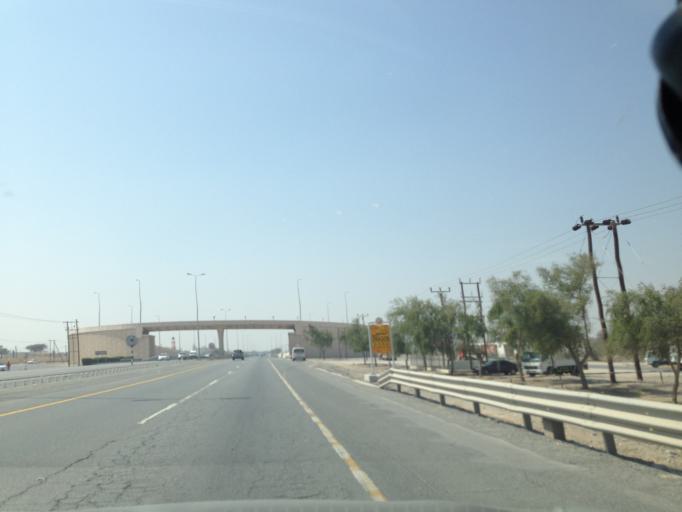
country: OM
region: Al Batinah
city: Barka'
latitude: 23.6637
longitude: 57.9497
